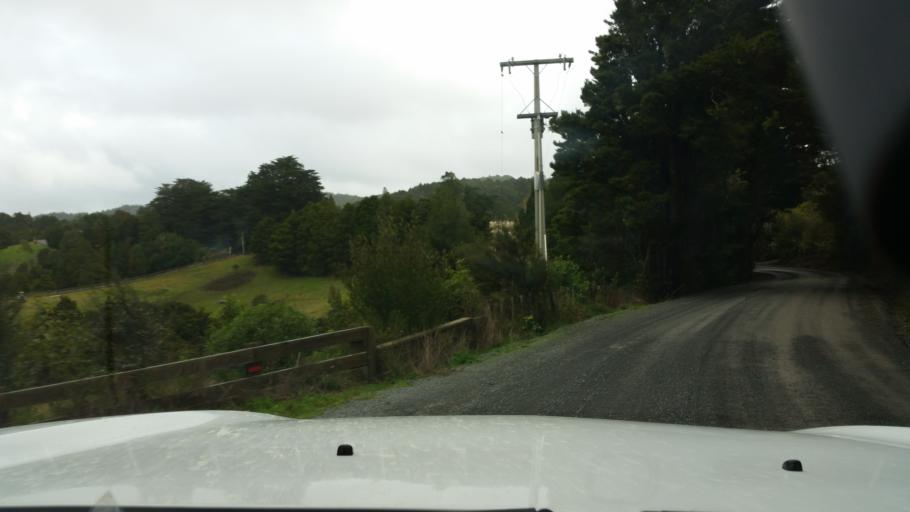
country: NZ
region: Northland
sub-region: Whangarei
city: Whangarei
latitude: -35.7319
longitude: 174.4276
